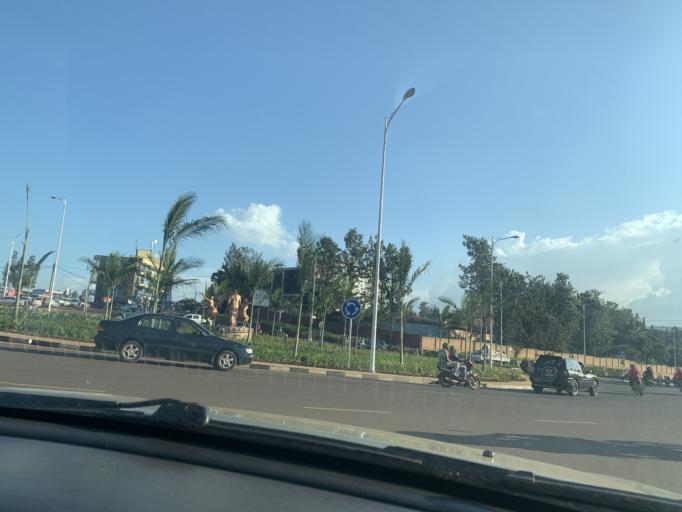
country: RW
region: Kigali
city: Kigali
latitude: -1.9669
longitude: 30.1024
